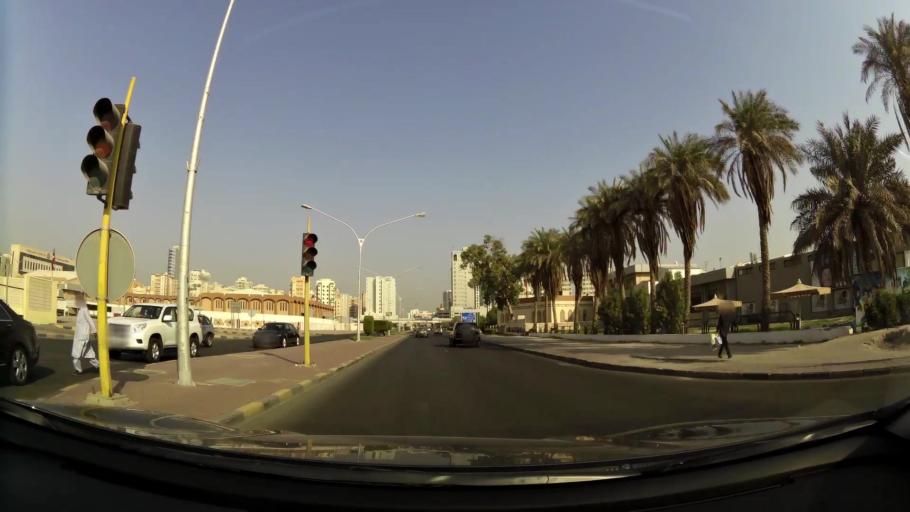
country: KW
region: Muhafazat Hawalli
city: Hawalli
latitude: 29.3253
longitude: 48.0304
